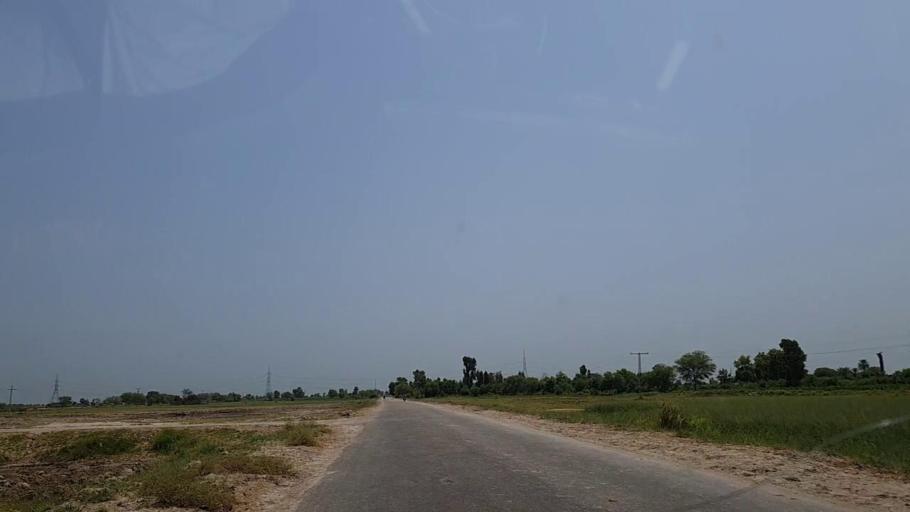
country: PK
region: Sindh
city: Ghotki
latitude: 27.9862
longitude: 69.3666
